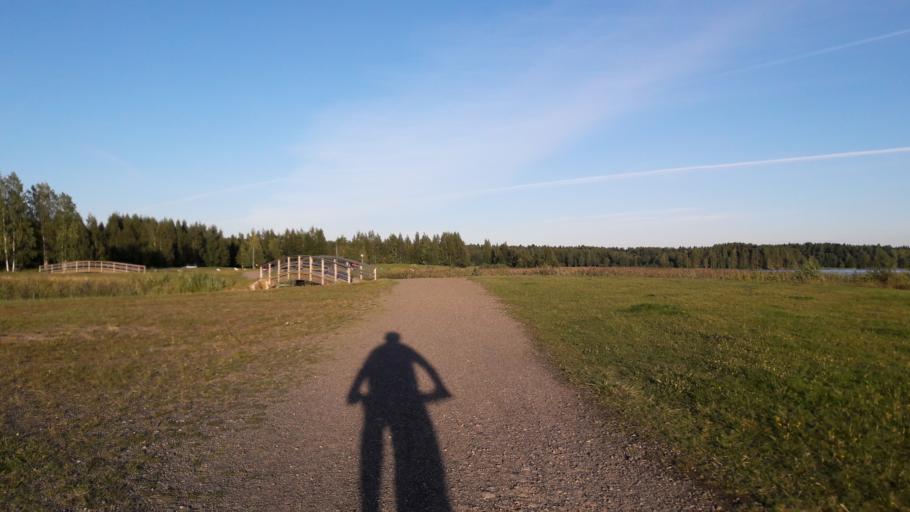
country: FI
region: North Karelia
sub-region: Joensuu
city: Joensuu
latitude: 62.6129
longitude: 29.7033
